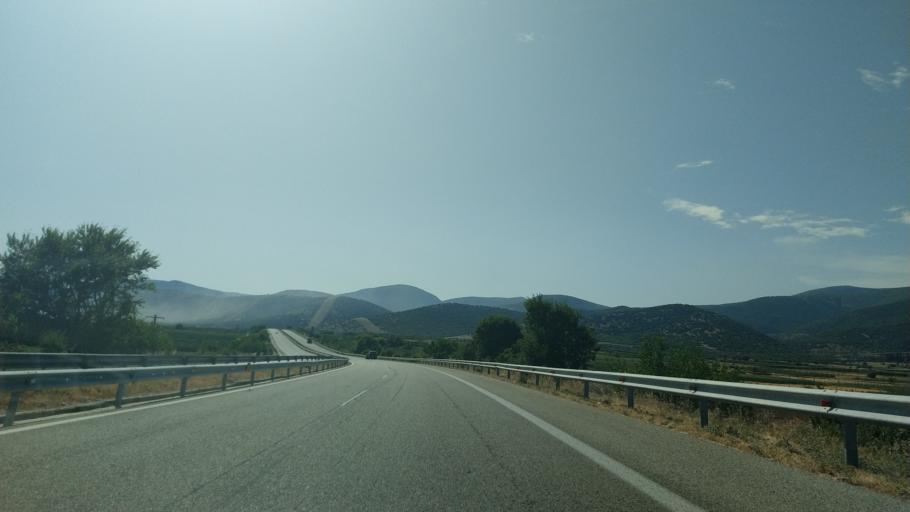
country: GR
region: East Macedonia and Thrace
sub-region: Nomos Kavalas
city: Nea Karvali
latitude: 40.9687
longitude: 24.5154
